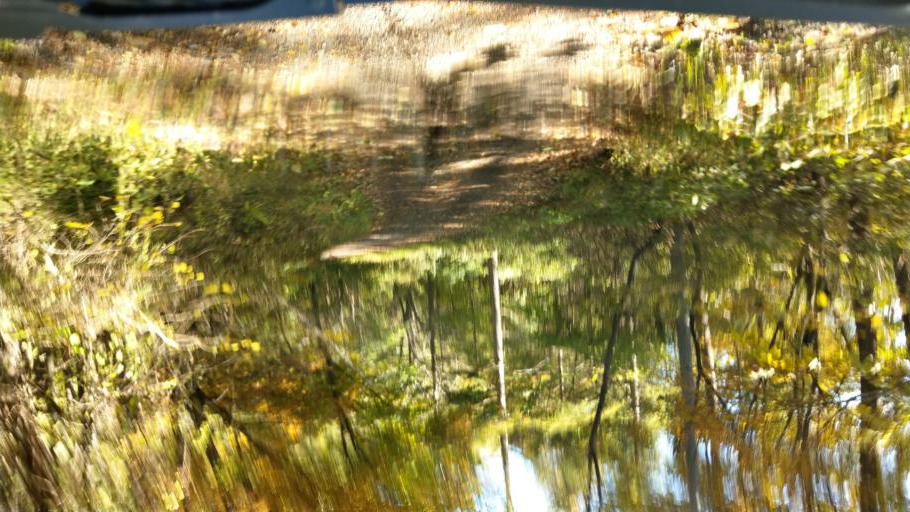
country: JP
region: Nagano
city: Komoro
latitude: 36.3784
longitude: 138.4287
